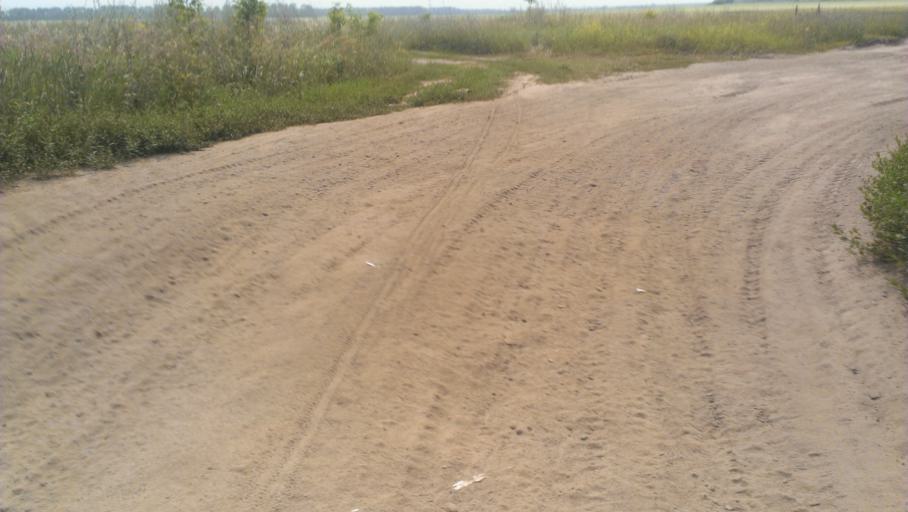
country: RU
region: Altai Krai
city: Gon'ba
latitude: 53.3811
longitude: 83.6309
